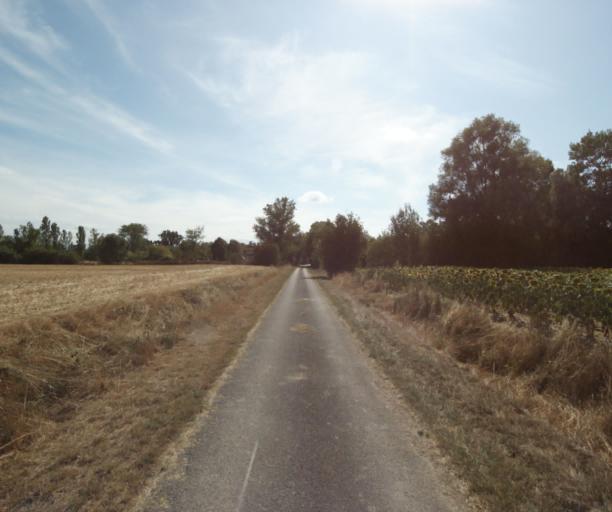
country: FR
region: Midi-Pyrenees
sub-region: Departement de la Haute-Garonne
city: Revel
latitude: 43.4922
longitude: 1.9876
